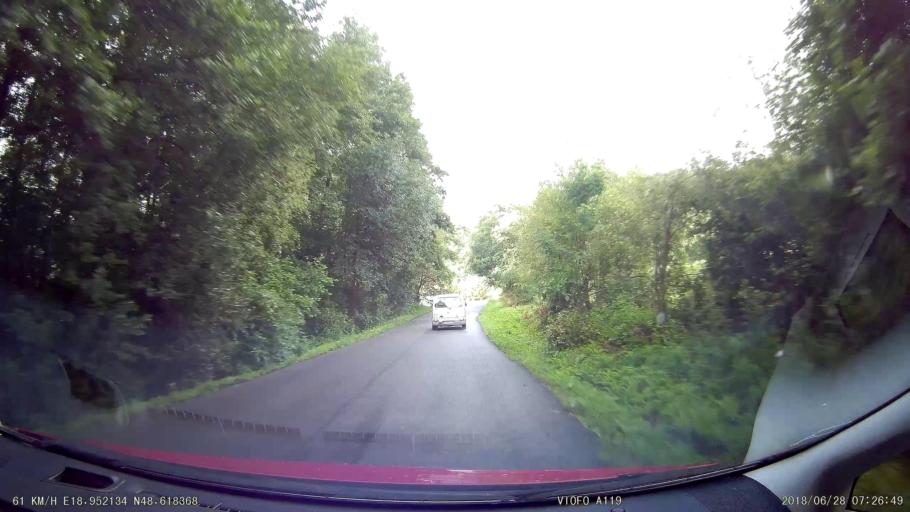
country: SK
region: Banskobystricky
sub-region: Okres Ziar nad Hronom
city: Kremnica
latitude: 48.6180
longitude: 18.9520
